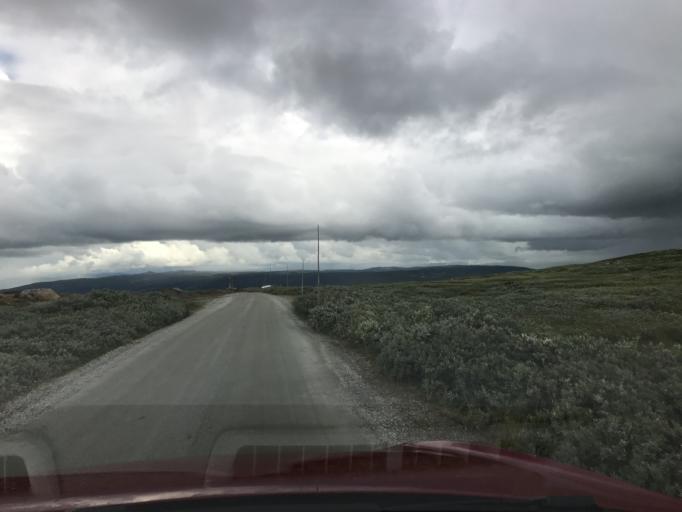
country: NO
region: Buskerud
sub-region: Hol
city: Geilo
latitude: 60.5461
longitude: 8.1410
